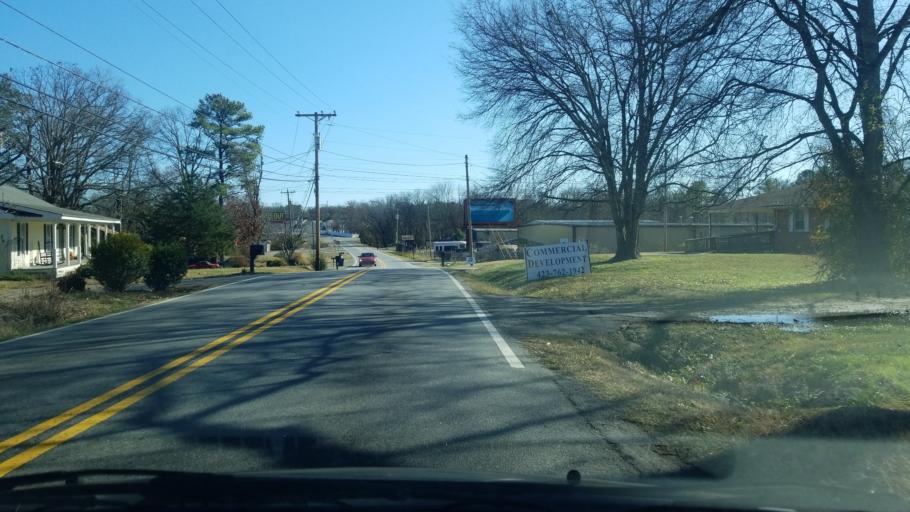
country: US
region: Georgia
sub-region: Catoosa County
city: Fort Oglethorpe
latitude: 34.9586
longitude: -85.2449
